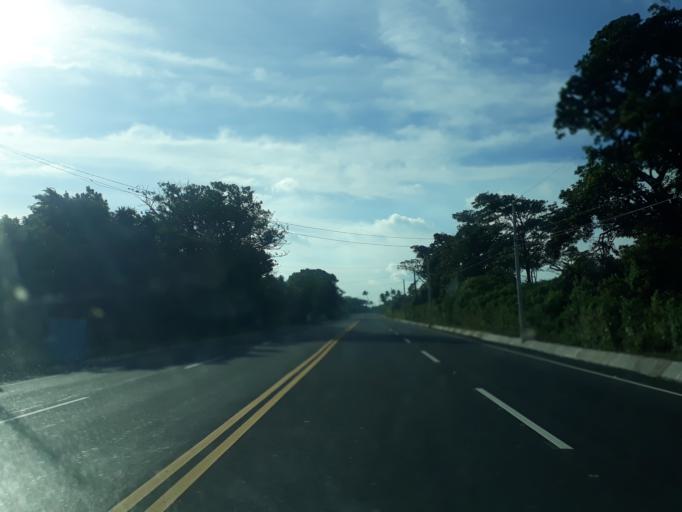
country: NI
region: Carazo
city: Diriamba
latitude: 11.9160
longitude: -86.2724
